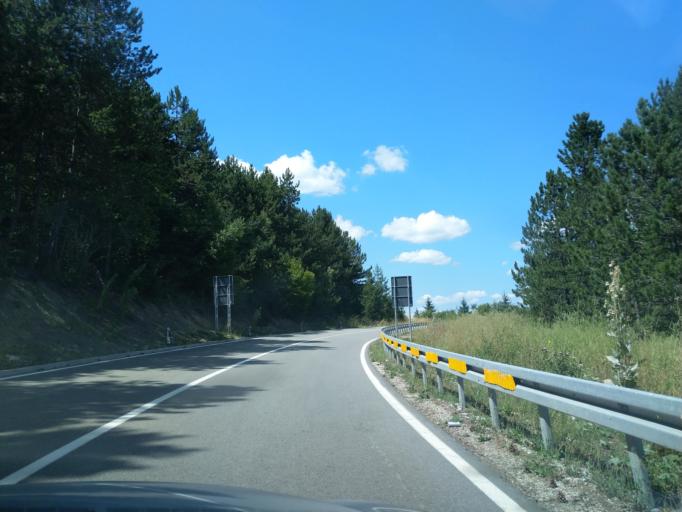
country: RS
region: Central Serbia
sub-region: Zlatiborski Okrug
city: Sjenica
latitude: 43.3092
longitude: 19.8986
